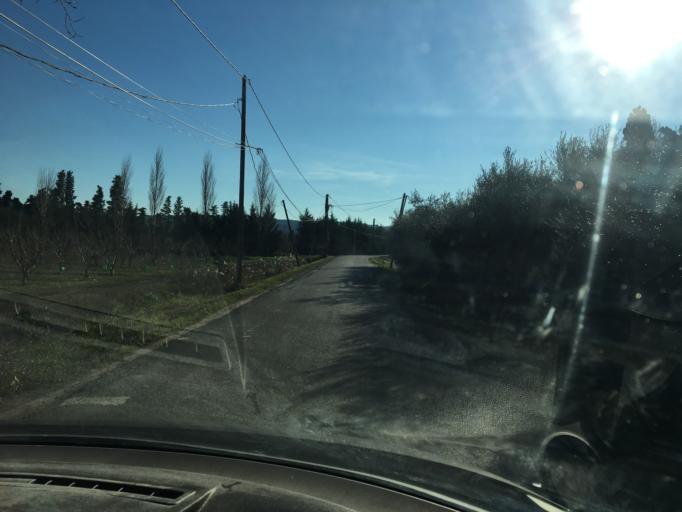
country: FR
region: Provence-Alpes-Cote d'Azur
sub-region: Departement des Bouches-du-Rhone
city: Maillane
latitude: 43.8143
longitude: 4.7875
